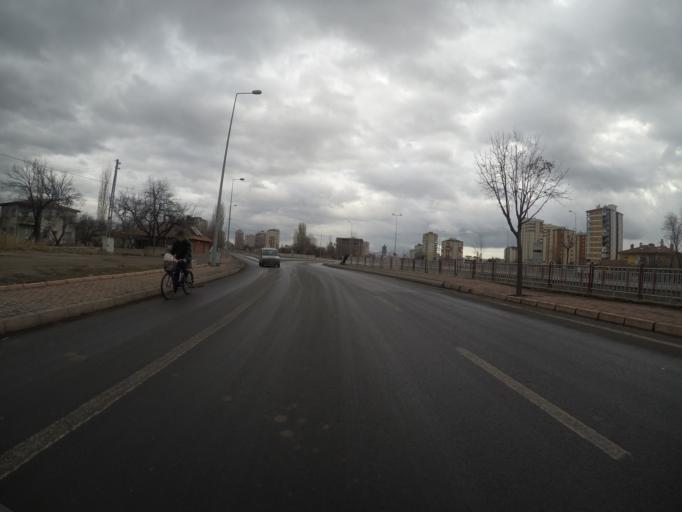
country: TR
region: Kayseri
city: Kayseri
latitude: 38.7501
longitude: 35.4735
